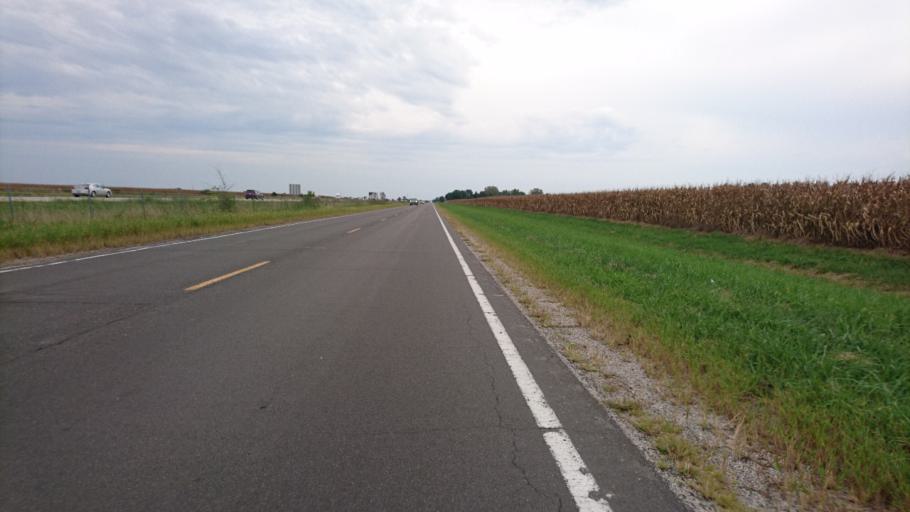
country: US
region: Illinois
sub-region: Sangamon County
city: Chatham
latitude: 39.6656
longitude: -89.6481
